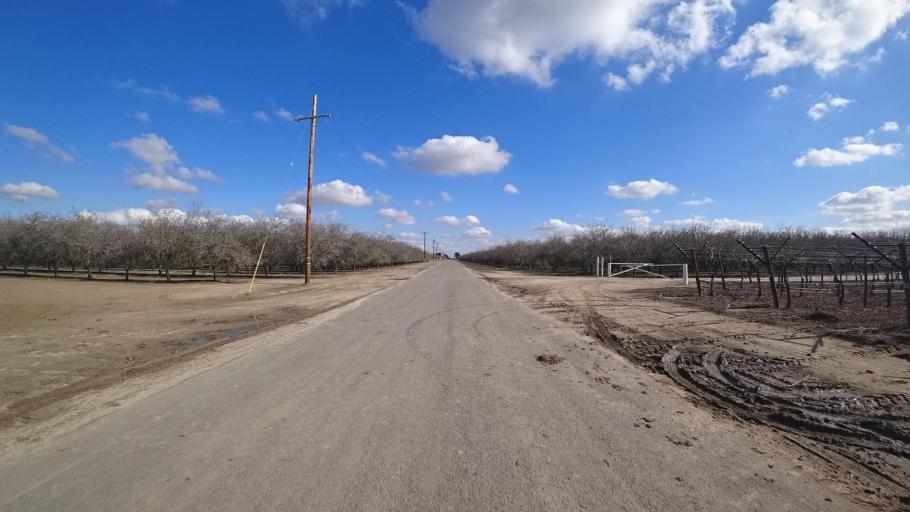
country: US
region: California
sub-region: Kern County
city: Delano
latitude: 35.7467
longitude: -119.3527
